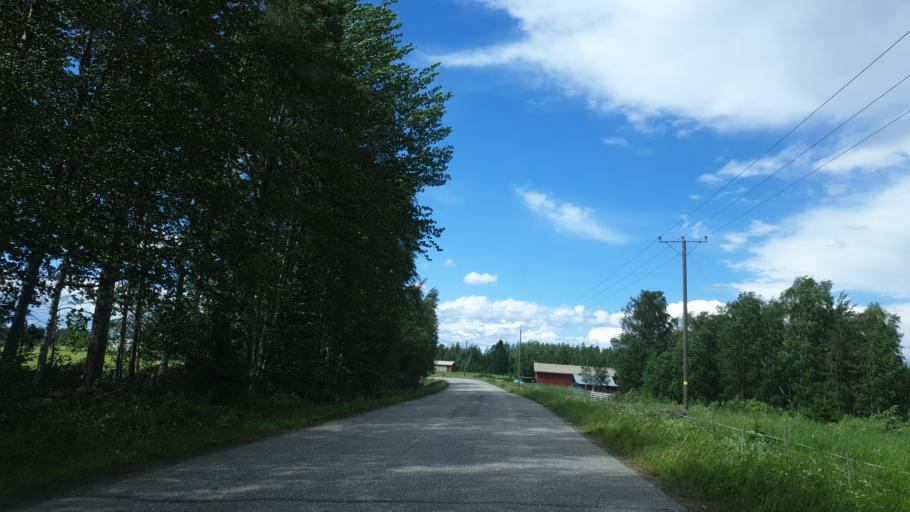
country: FI
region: Northern Savo
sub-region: Koillis-Savo
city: Kaavi
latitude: 62.9891
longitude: 28.7297
